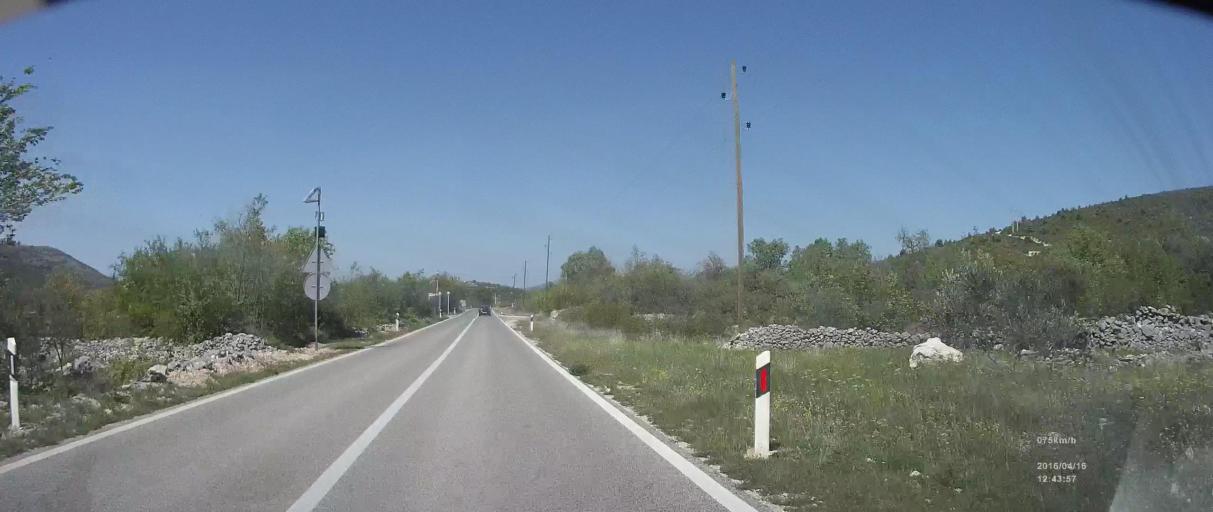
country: HR
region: Sibensko-Kniniska
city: Rogoznica
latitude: 43.6363
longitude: 16.0693
